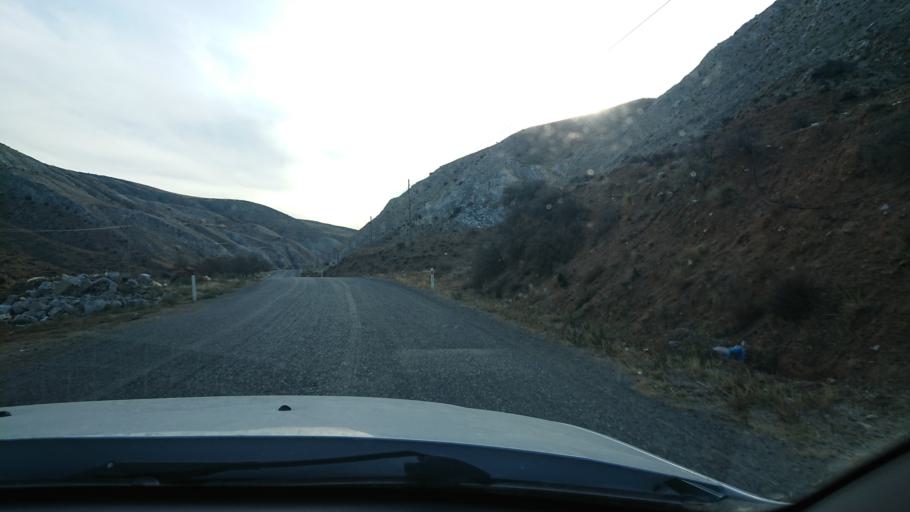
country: TR
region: Ankara
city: Sereflikochisar
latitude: 38.7557
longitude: 33.6935
